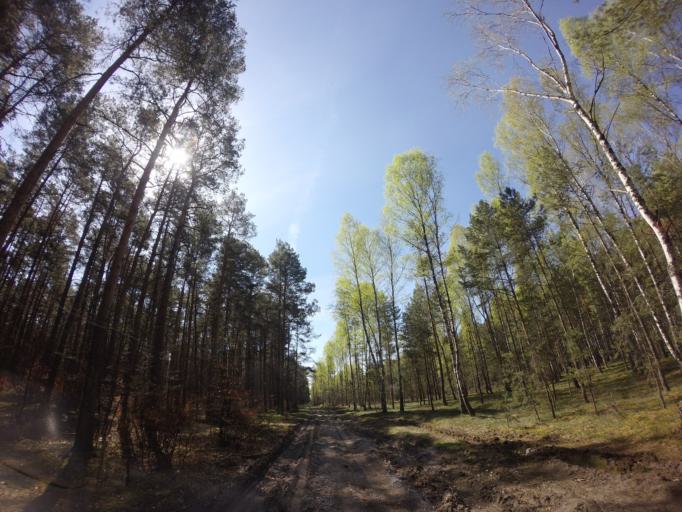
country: PL
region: West Pomeranian Voivodeship
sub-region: Powiat drawski
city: Kalisz Pomorski
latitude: 53.2038
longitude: 15.9377
